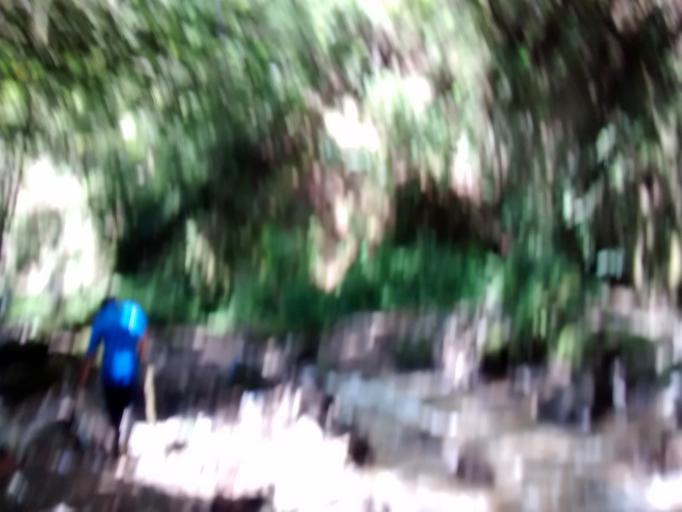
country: GT
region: Sacatepequez
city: Santo Domingo Xenacoj
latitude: 14.6960
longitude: -90.7256
